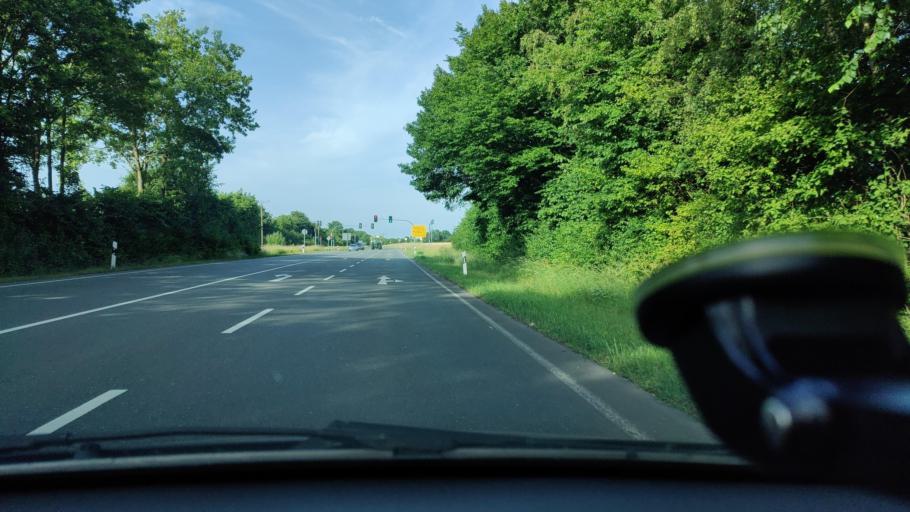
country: DE
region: North Rhine-Westphalia
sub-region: Regierungsbezirk Munster
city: Coesfeld
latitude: 52.0136
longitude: 7.2145
